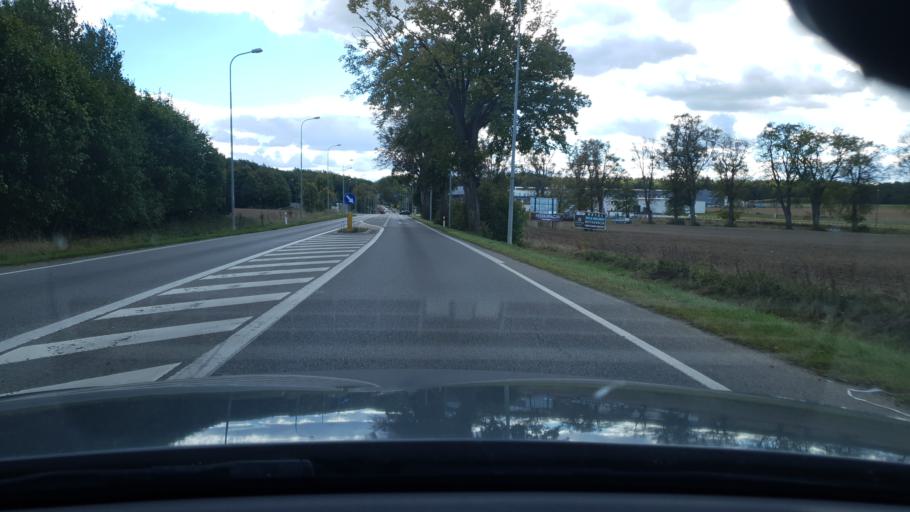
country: PL
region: Pomeranian Voivodeship
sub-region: Powiat wejherowski
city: Rekowo Dolne
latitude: 54.6399
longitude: 18.3462
